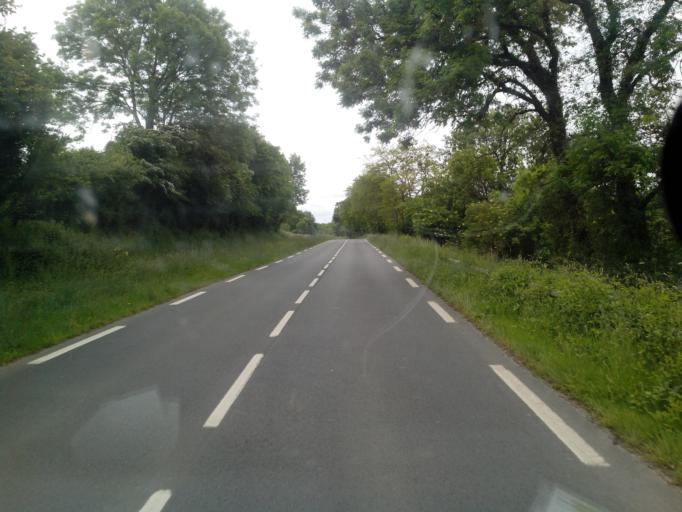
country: FR
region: Lower Normandy
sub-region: Departement du Calvados
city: Amfreville
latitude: 49.2587
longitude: -0.2374
